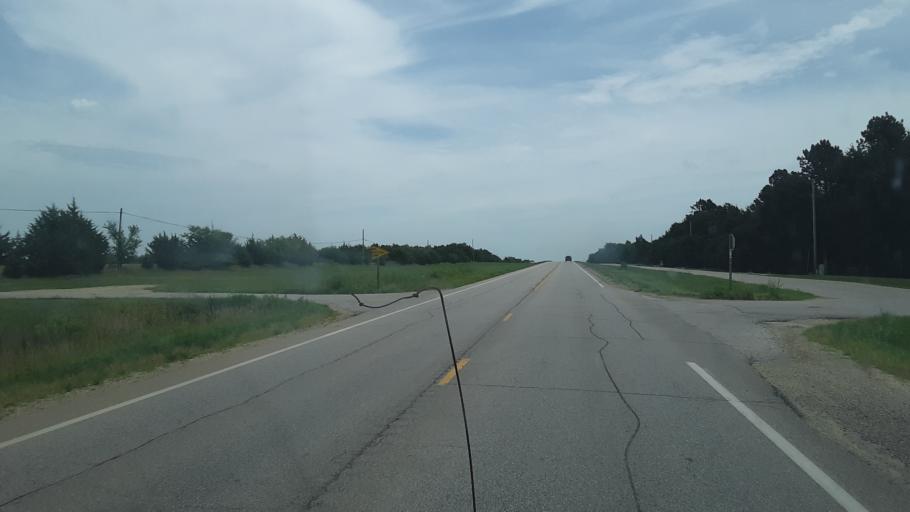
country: US
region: Kansas
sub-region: Butler County
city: El Dorado
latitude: 37.8105
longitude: -96.7476
